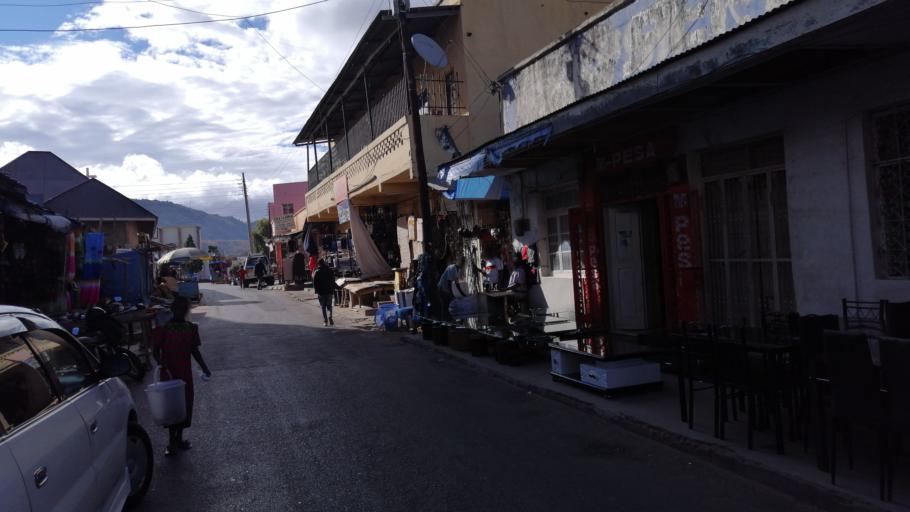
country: TZ
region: Iringa
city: Iringa
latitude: -7.7826
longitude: 35.6960
